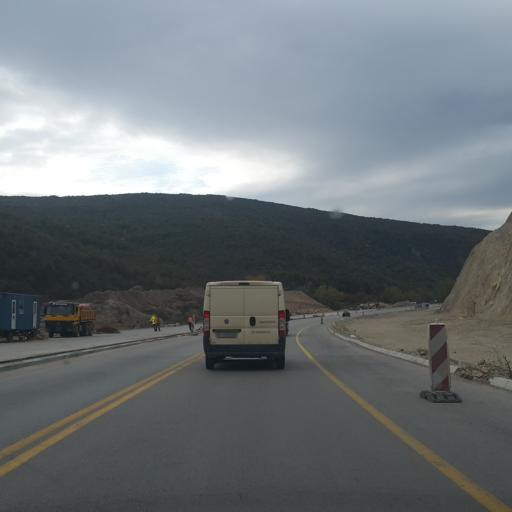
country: RS
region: Central Serbia
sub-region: Pirotski Okrug
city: Bela Palanka
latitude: 43.2250
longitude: 22.4295
